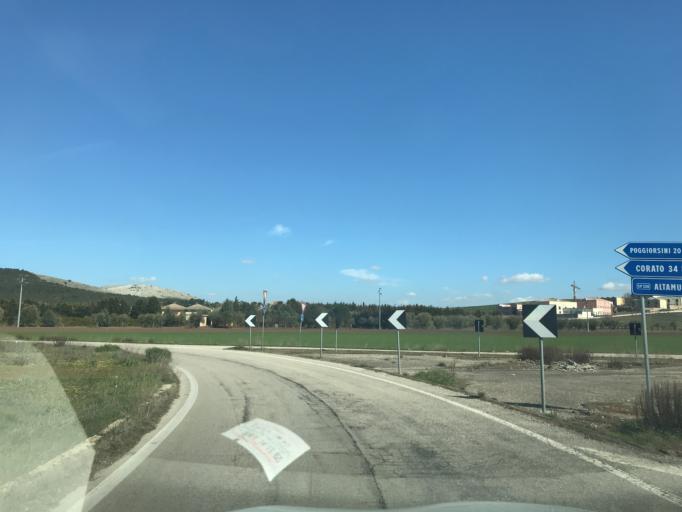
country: IT
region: Apulia
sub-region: Provincia di Bari
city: Gravina in Puglia
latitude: 40.8606
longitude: 16.4368
